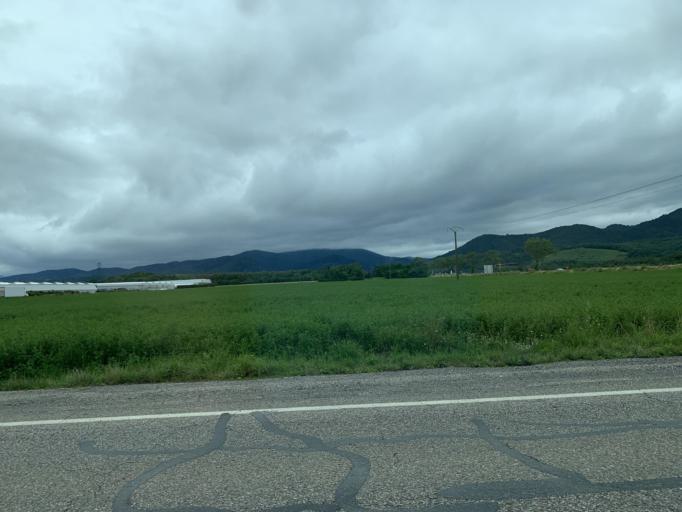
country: FR
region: Alsace
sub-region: Departement du Haut-Rhin
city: Cernay
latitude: 47.7947
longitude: 7.1580
